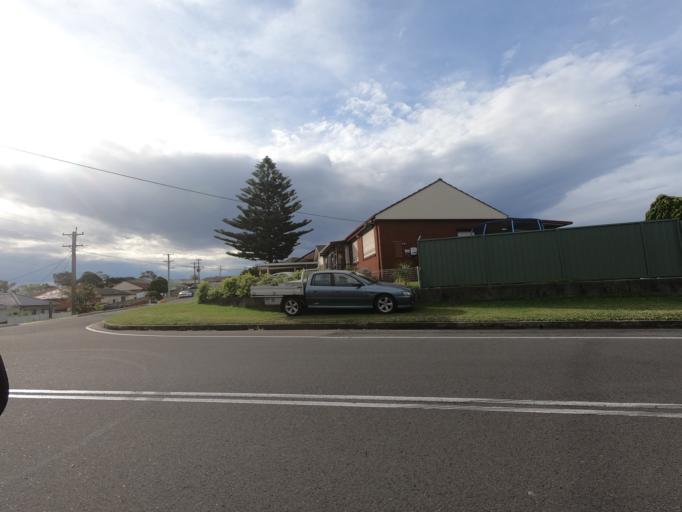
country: AU
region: New South Wales
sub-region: Wollongong
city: Lake Heights
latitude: -34.4867
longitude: 150.8686
